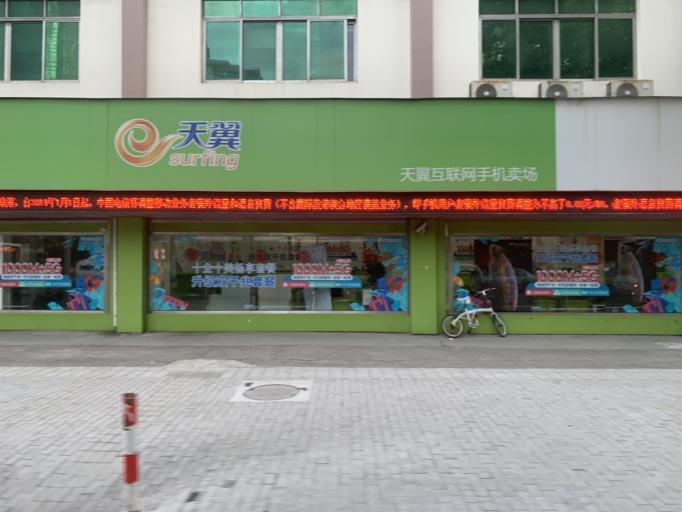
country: CN
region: Shanghai Shi
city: Pudong
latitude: 31.2255
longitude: 121.5232
